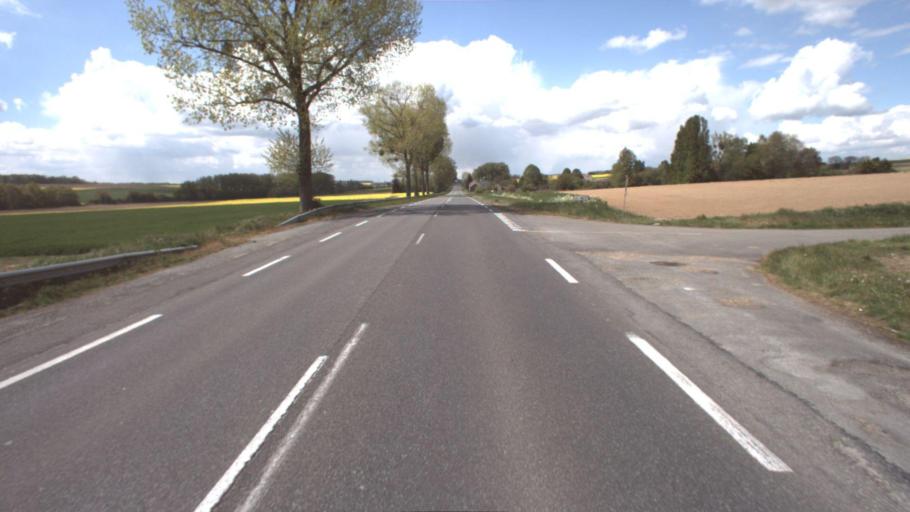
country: FR
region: Ile-de-France
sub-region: Departement de Seine-et-Marne
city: La Ferte-Gaucher
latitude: 48.6940
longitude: 3.3147
